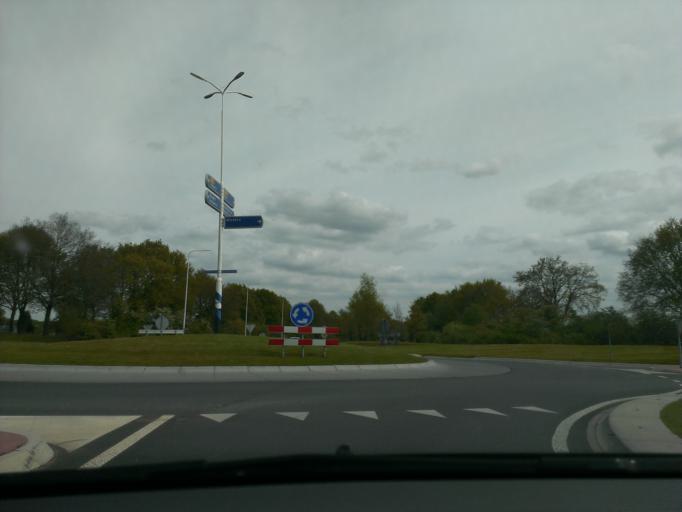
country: NL
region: Gelderland
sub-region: Gemeente Epe
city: Epe
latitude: 52.3485
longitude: 5.9627
